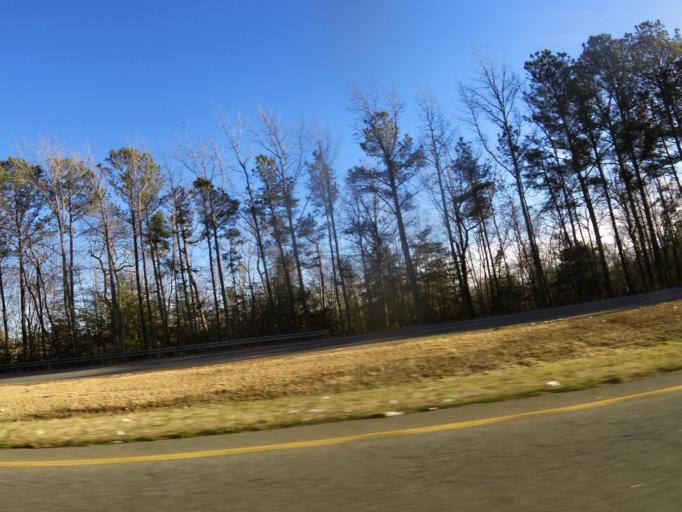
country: US
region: Virginia
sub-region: Isle of Wight County
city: Windsor
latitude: 36.6775
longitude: -76.7761
